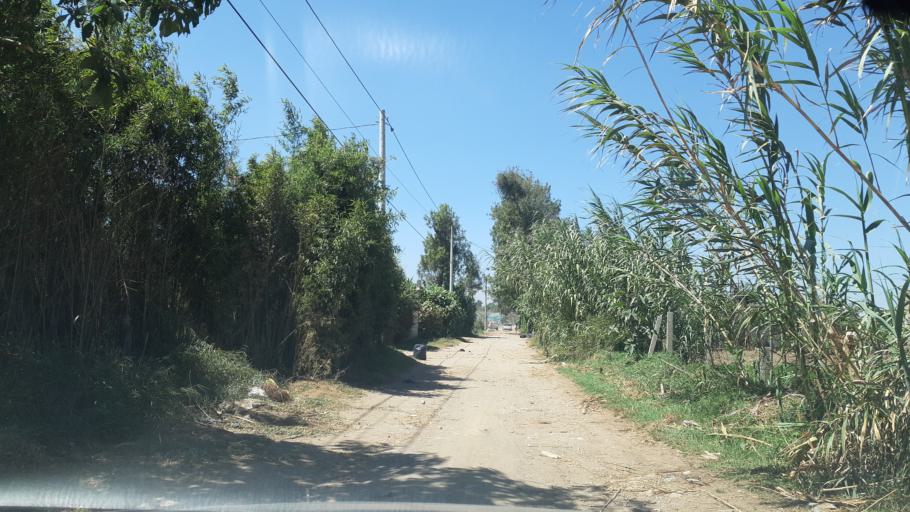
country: GT
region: Chimaltenango
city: El Tejar
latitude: 14.6457
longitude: -90.8086
